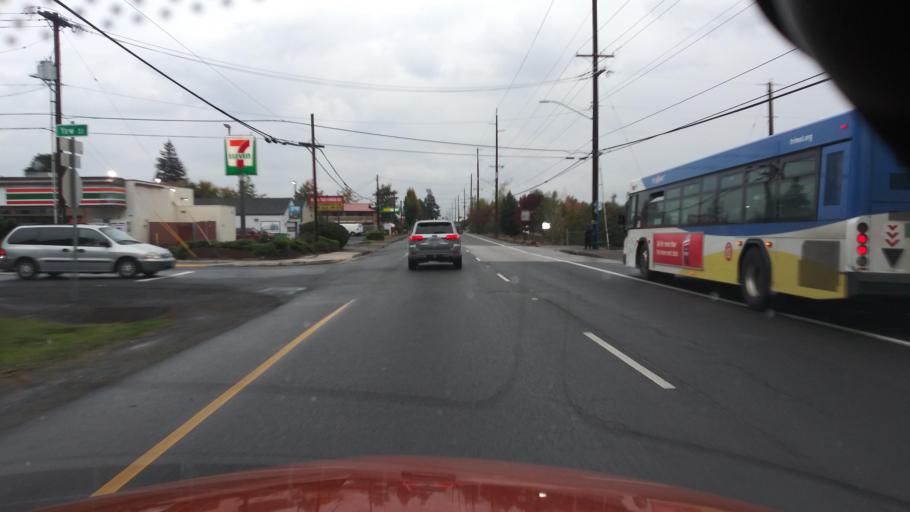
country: US
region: Oregon
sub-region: Washington County
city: Cornelius
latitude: 45.5202
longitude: -123.0737
